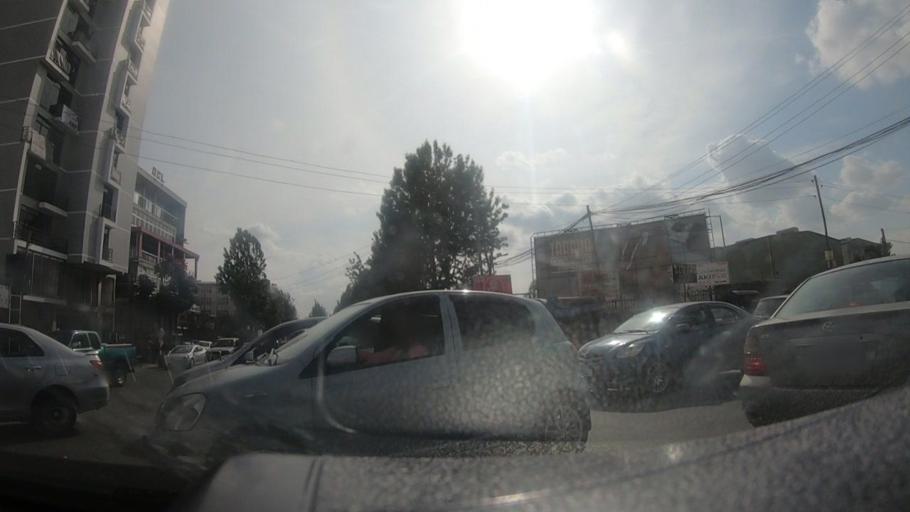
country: ET
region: Adis Abeba
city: Addis Ababa
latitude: 9.0112
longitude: 38.8213
